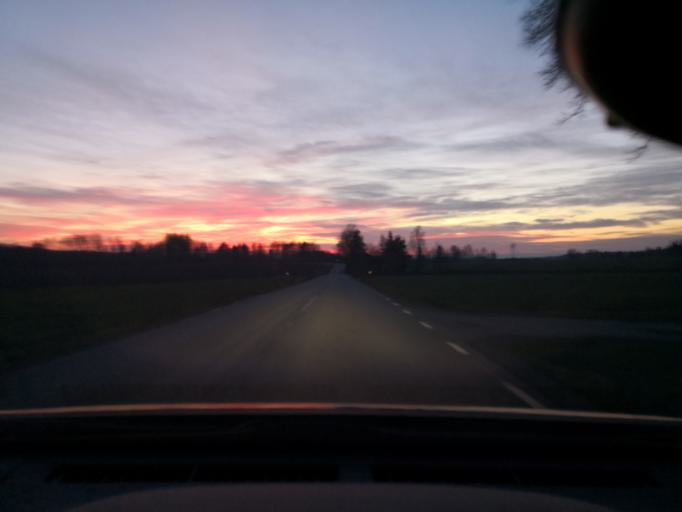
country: SE
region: OErebro
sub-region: Lindesbergs Kommun
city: Frovi
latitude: 59.3409
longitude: 15.3868
